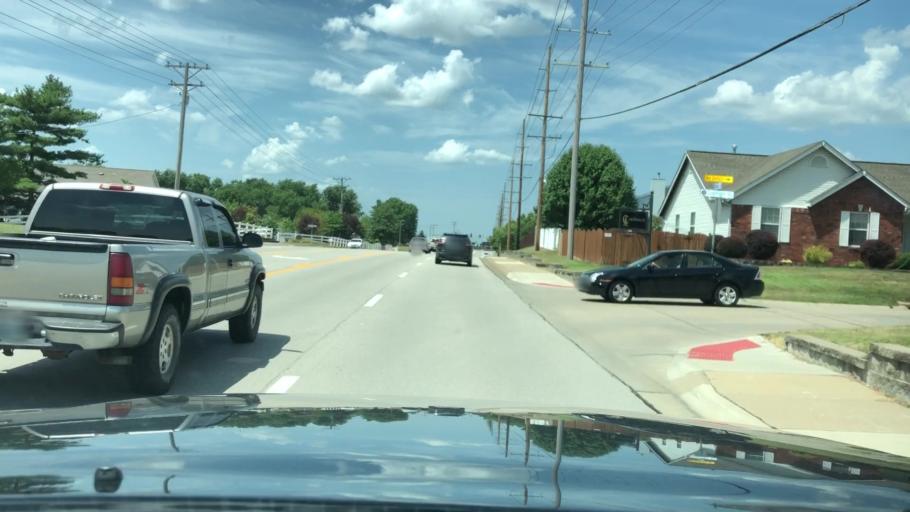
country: US
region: Missouri
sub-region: Saint Charles County
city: O'Fallon
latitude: 38.7874
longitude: -90.6661
